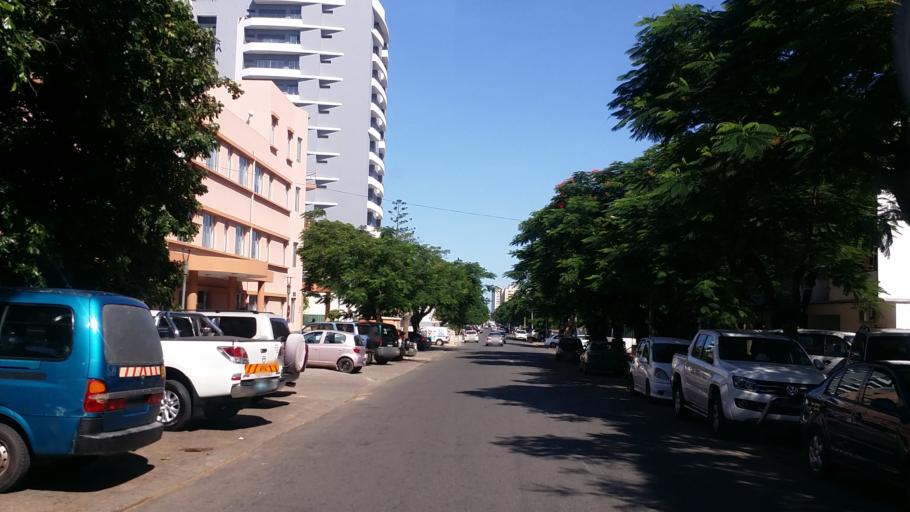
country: MZ
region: Maputo City
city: Maputo
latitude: -25.9708
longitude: 32.5852
